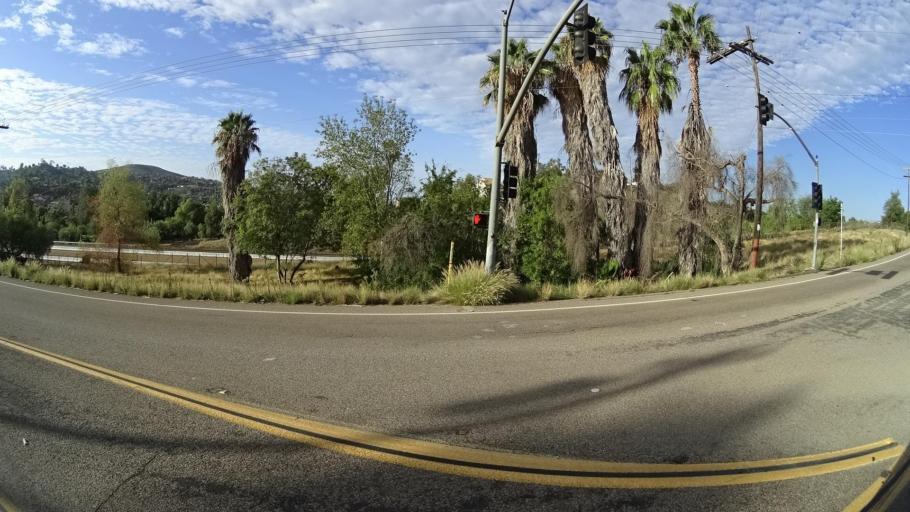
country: US
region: California
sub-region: San Diego County
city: Spring Valley
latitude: 32.7492
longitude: -116.9947
